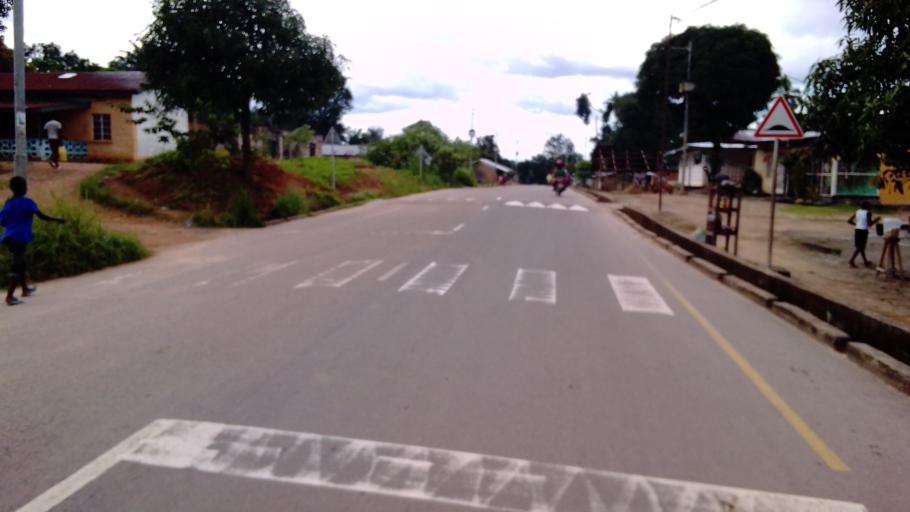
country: SL
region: Eastern Province
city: Koidu
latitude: 8.6557
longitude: -10.9757
